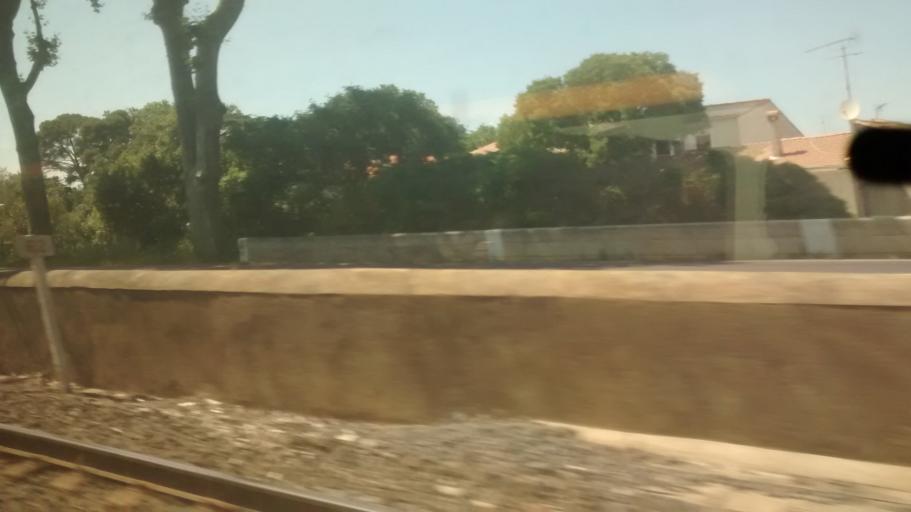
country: FR
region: Languedoc-Roussillon
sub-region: Departement de l'Herault
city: Saint-Bres
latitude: 43.6624
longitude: 4.0321
